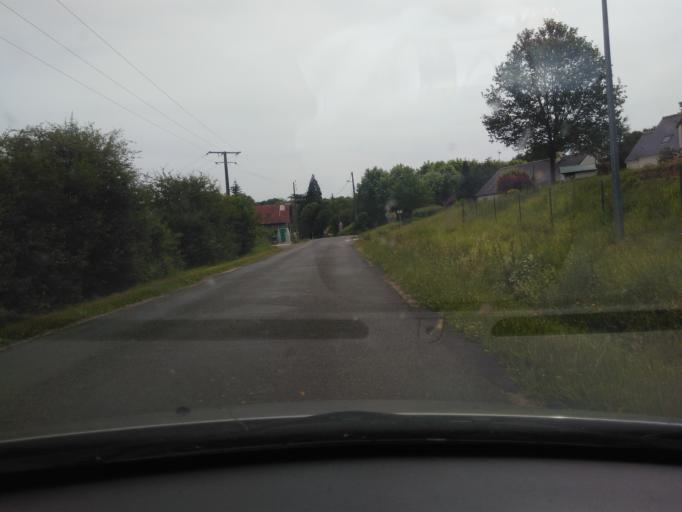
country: FR
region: Centre
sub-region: Departement d'Indre-et-Loire
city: Charge
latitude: 47.4077
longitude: 1.0480
